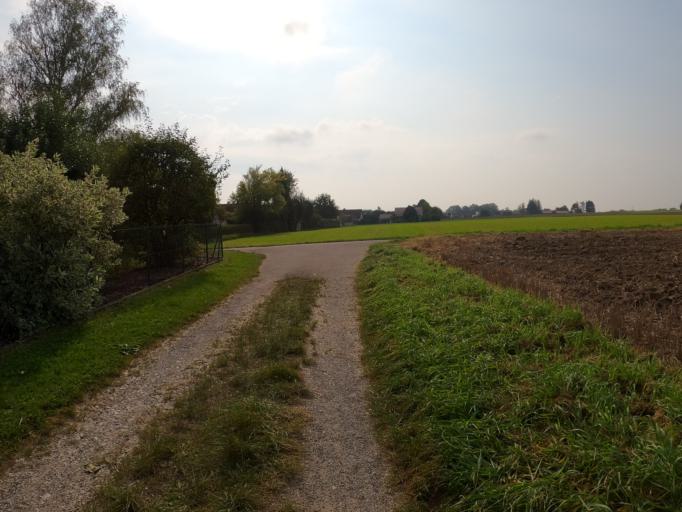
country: DE
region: Bavaria
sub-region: Swabia
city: Offingen
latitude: 48.4845
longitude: 10.3573
